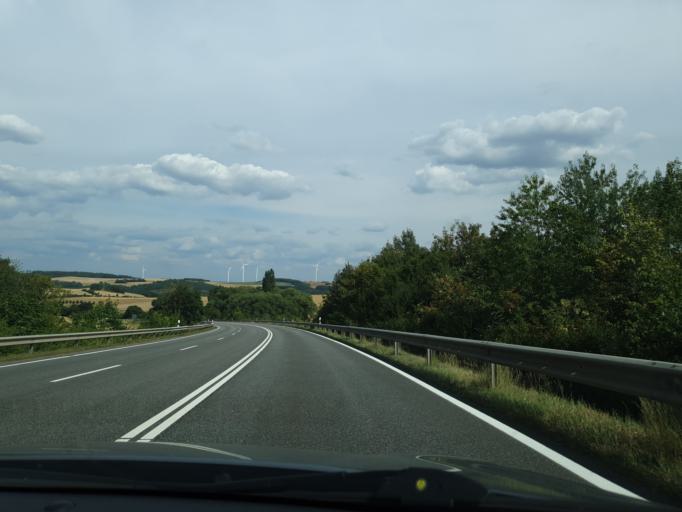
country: DE
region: Rheinland-Pfalz
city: Mayen
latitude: 50.3089
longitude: 7.2084
